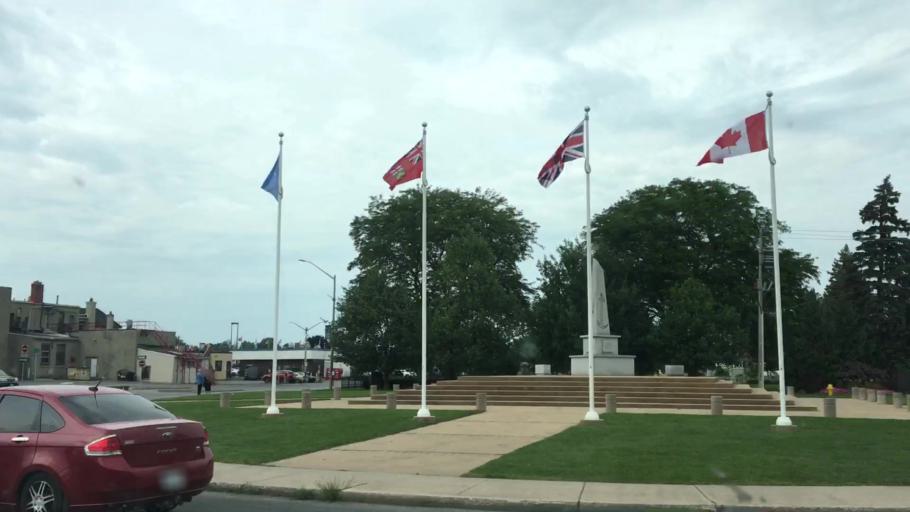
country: CA
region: Ontario
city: Quinte West
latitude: 44.1001
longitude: -77.5757
